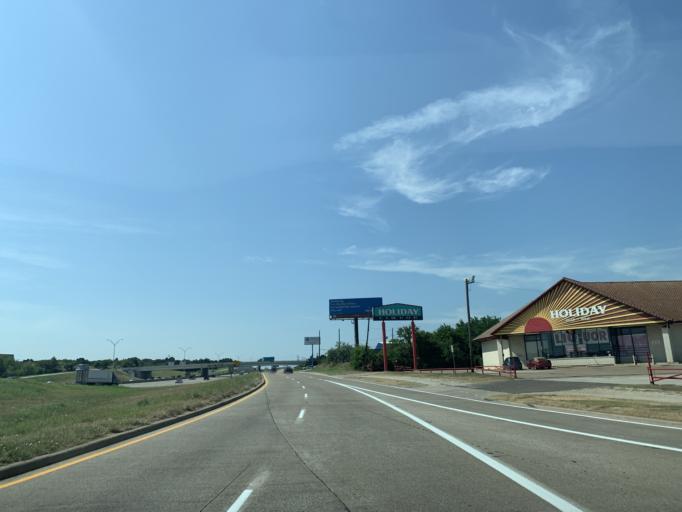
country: US
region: Texas
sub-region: Tarrant County
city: Edgecliff Village
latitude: 32.6637
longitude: -97.3220
